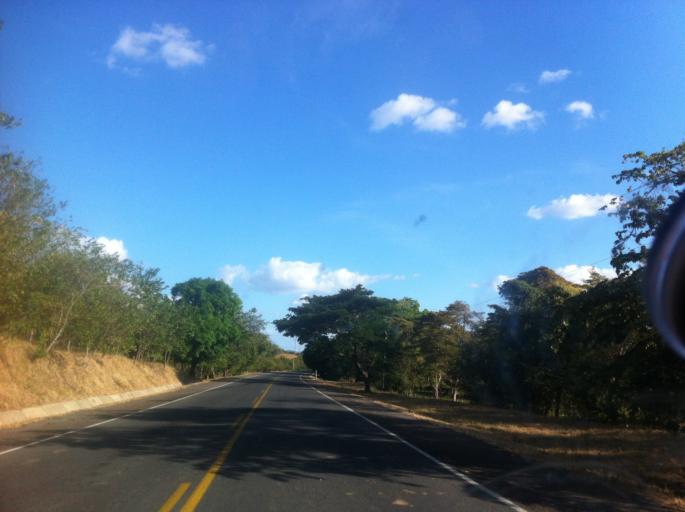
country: NI
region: Chontales
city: Acoyapa
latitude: 11.9397
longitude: -85.1470
